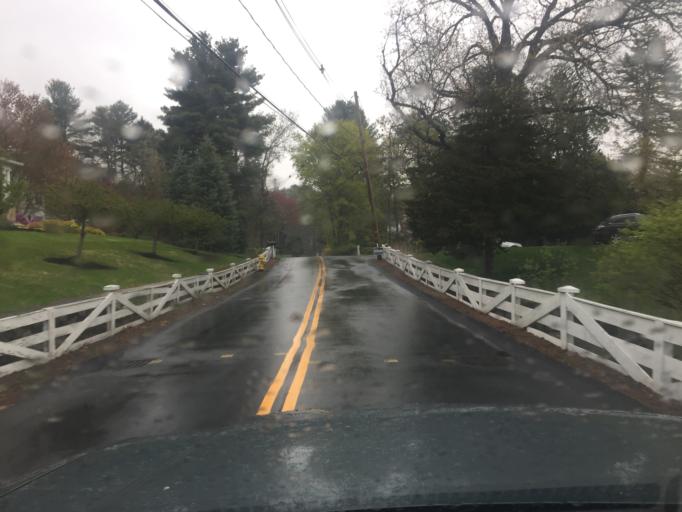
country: US
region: Massachusetts
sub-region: Norfolk County
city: Westwood
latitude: 42.2297
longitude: -71.2284
